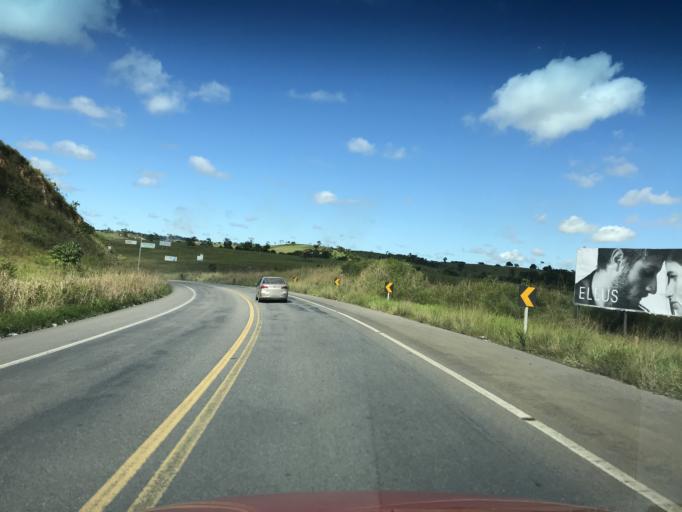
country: BR
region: Bahia
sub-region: Conceicao Do Almeida
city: Muritiba
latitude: -12.9315
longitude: -39.2537
